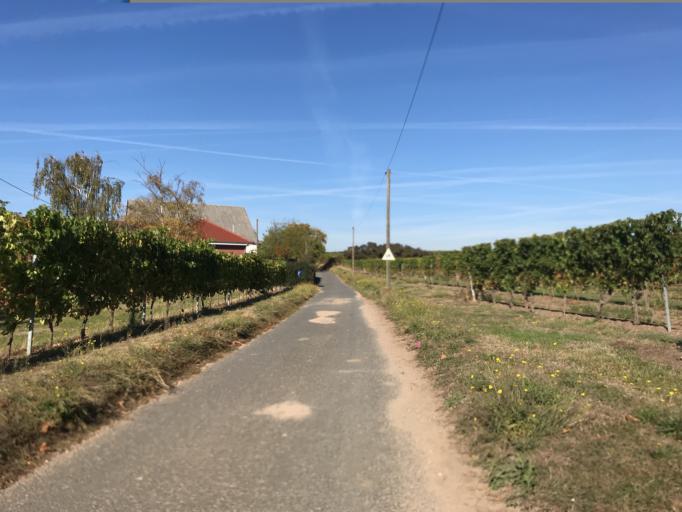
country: DE
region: Hesse
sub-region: Regierungsbezirk Darmstadt
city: Hochheim am Main
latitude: 50.0129
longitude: 8.3115
